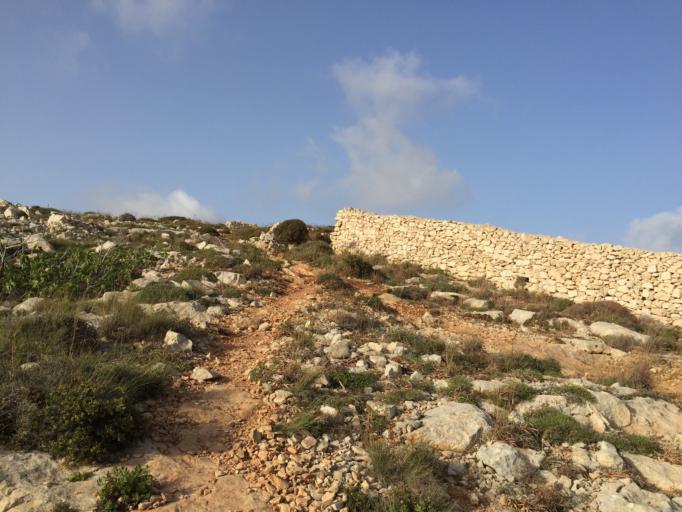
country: MT
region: Il-Qrendi
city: Qrendi
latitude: 35.8252
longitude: 14.4408
